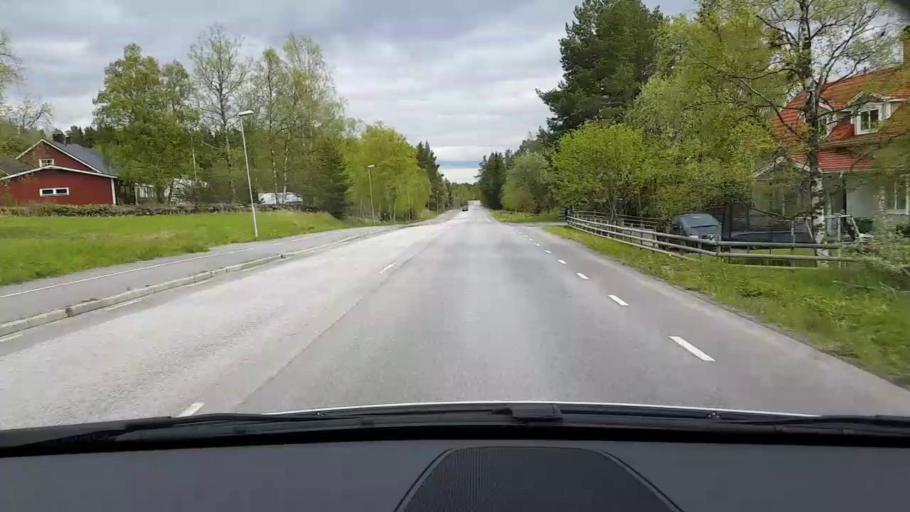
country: SE
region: Jaemtland
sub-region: OEstersunds Kommun
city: Brunflo
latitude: 63.1119
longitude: 14.7902
